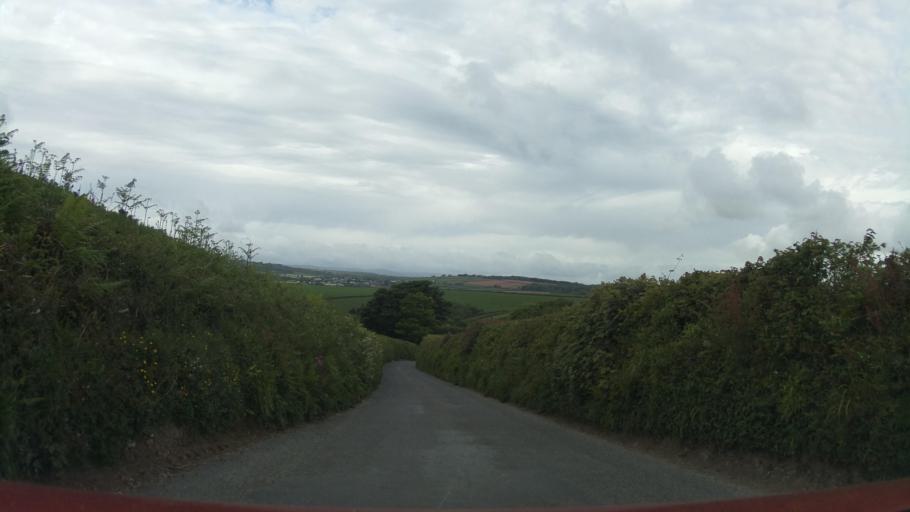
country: GB
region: England
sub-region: Devon
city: Dartmouth
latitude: 50.3296
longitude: -3.6440
